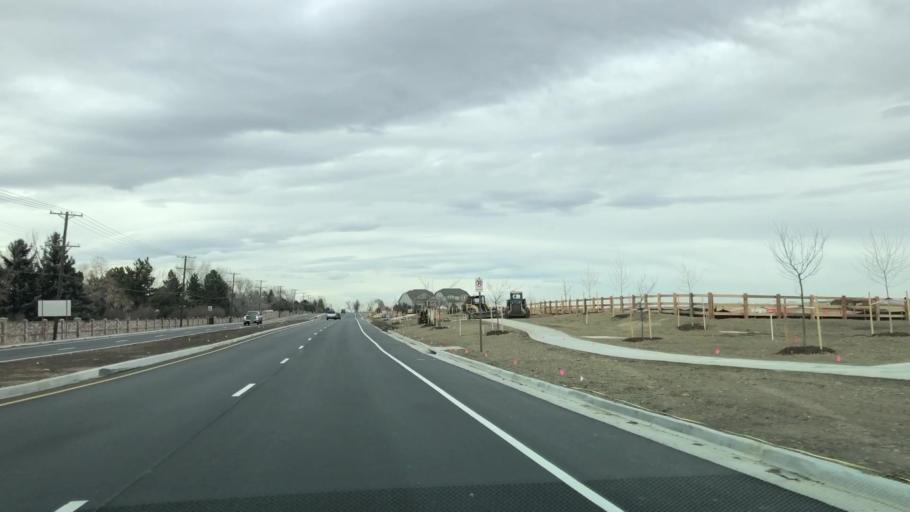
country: US
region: Colorado
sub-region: Larimer County
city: Loveland
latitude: 40.4210
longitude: -105.0208
